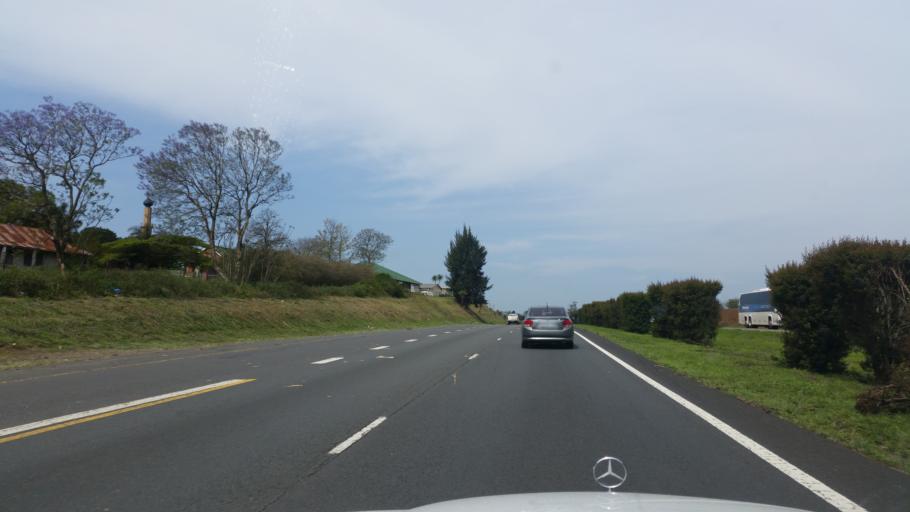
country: ZA
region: KwaZulu-Natal
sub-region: uMgungundlovu District Municipality
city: Camperdown
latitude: -29.7303
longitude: 30.5432
